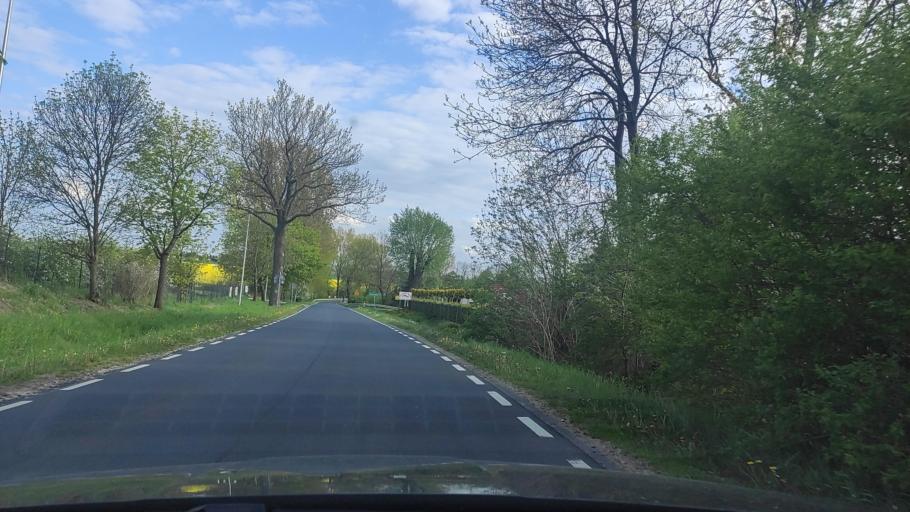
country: PL
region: Greater Poland Voivodeship
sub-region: Powiat poznanski
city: Kostrzyn
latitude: 52.4203
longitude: 17.2268
